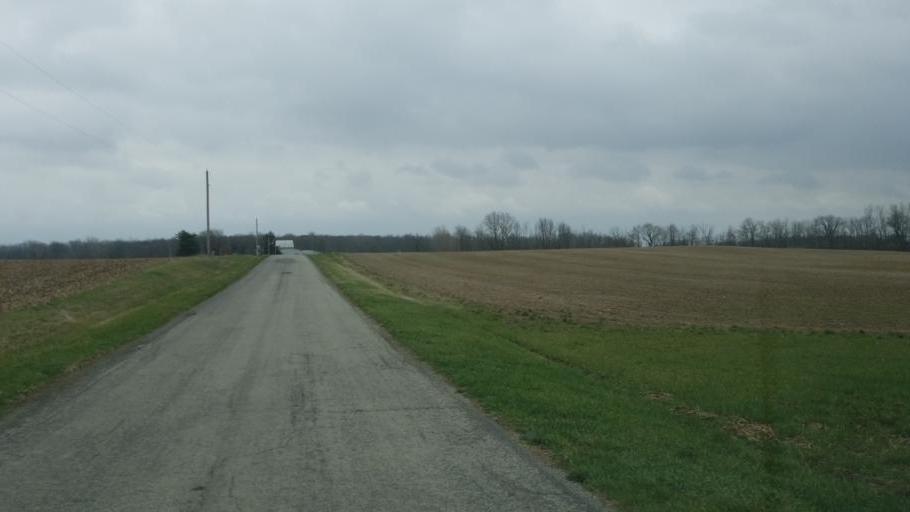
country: US
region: Ohio
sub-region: Union County
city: Richwood
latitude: 40.4133
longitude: -83.3630
